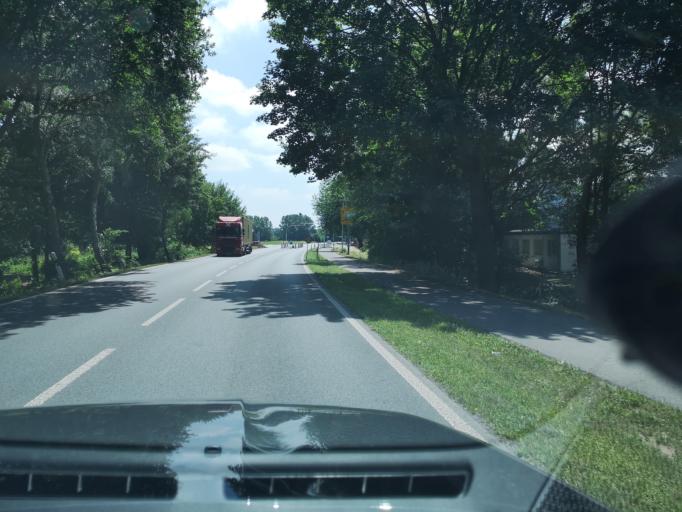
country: DE
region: North Rhine-Westphalia
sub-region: Regierungsbezirk Dusseldorf
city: Emmerich
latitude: 51.8400
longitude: 6.2757
